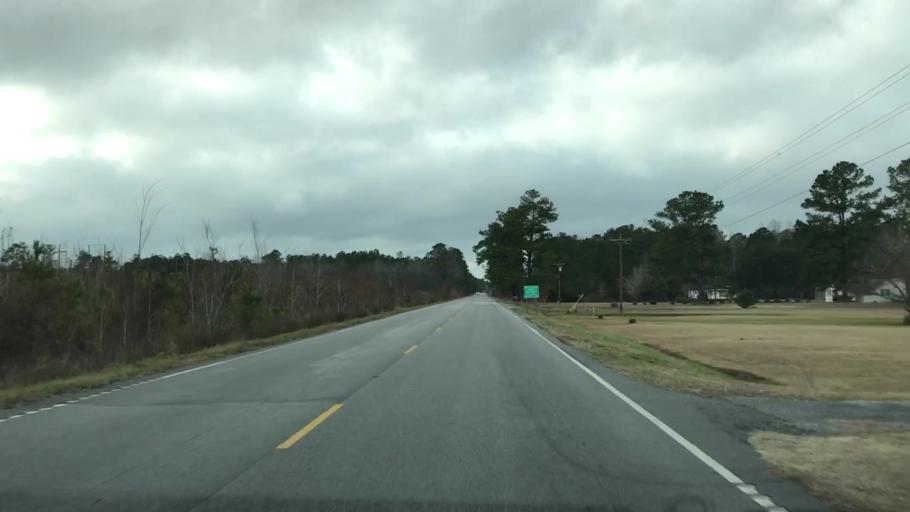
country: US
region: South Carolina
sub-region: Berkeley County
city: Saint Stephen
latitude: 33.2828
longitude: -79.7383
